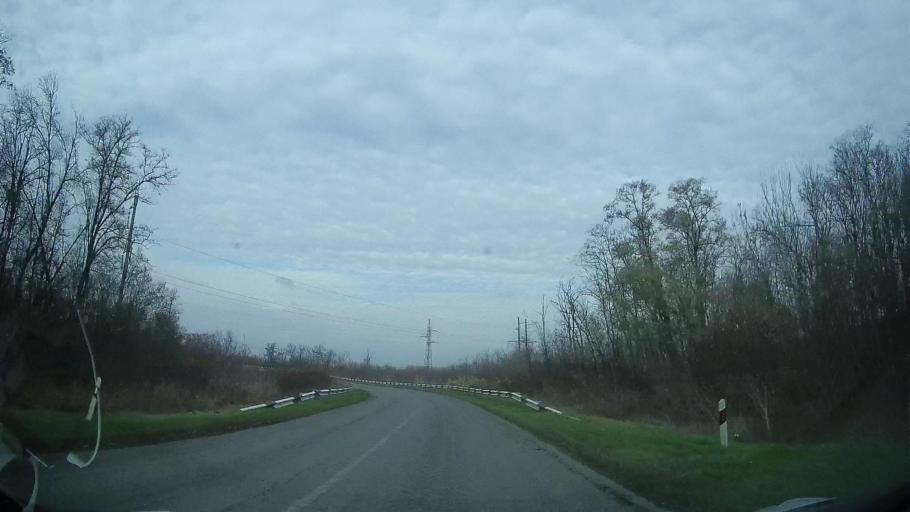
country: RU
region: Rostov
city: Zernograd
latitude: 46.8836
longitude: 40.3413
